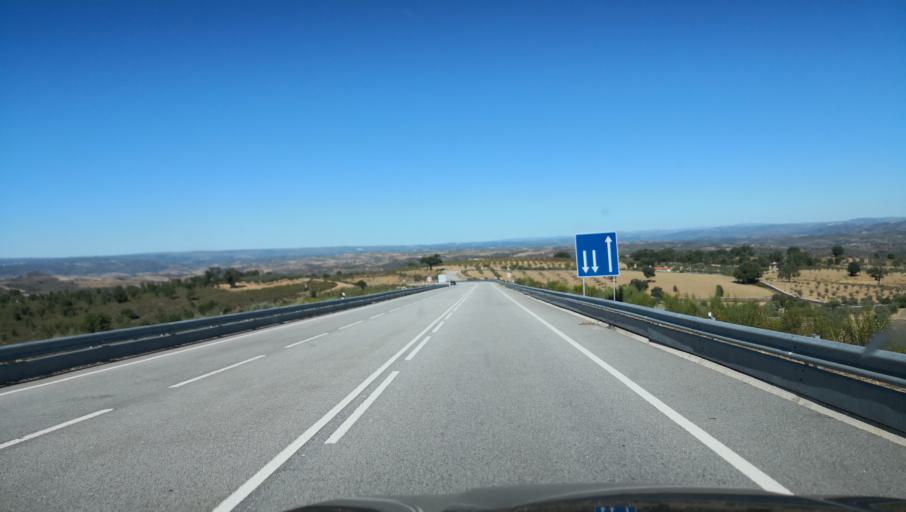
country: PT
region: Braganca
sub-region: Mirandela
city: Mirandela
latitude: 41.4851
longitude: -7.2240
